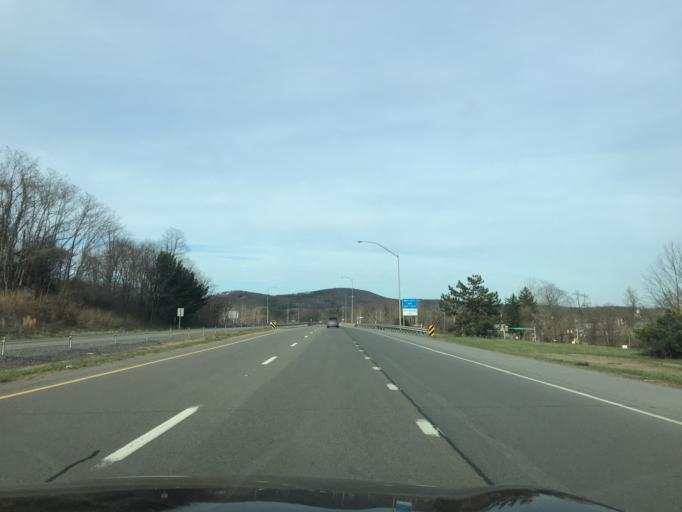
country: US
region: Pennsylvania
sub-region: Lycoming County
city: Montoursville
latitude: 41.2493
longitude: -76.9394
